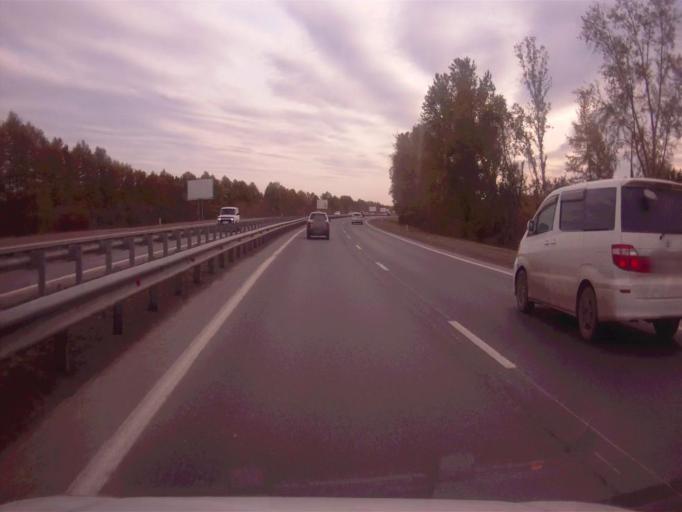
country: RU
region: Chelyabinsk
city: Novosineglazovskiy
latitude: 55.0284
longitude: 61.4487
